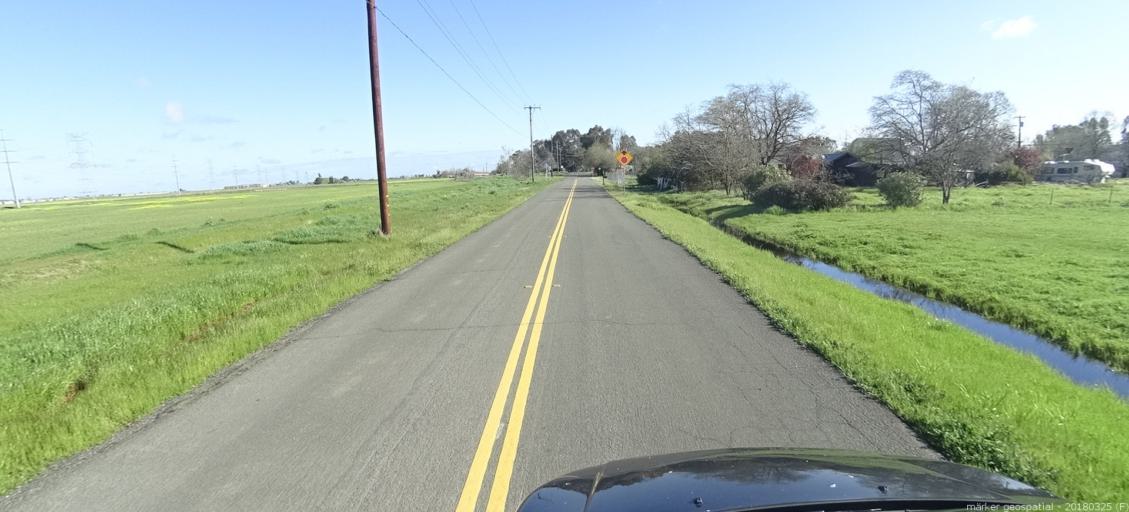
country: US
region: California
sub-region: Sacramento County
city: Rio Linda
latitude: 38.6617
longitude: -121.4851
